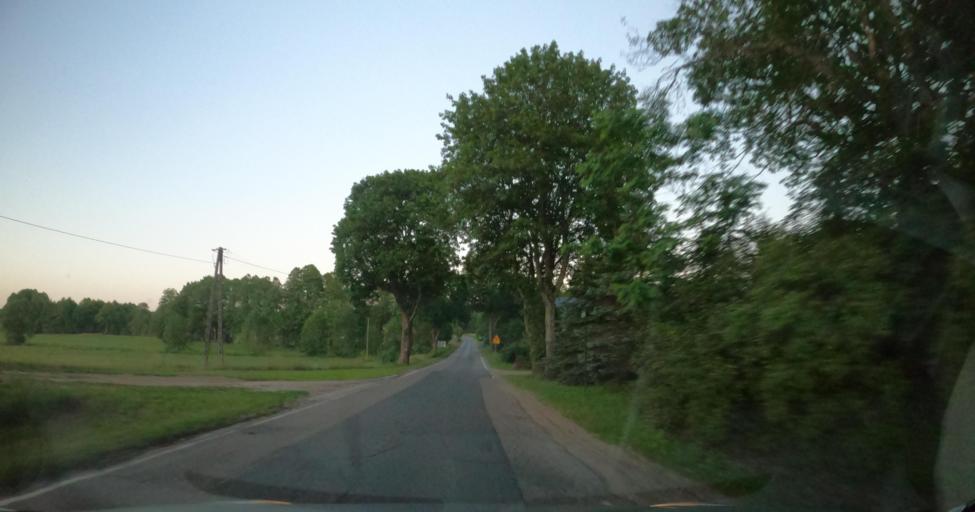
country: PL
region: Pomeranian Voivodeship
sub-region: Powiat wejherowski
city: Luzino
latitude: 54.4666
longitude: 18.0968
